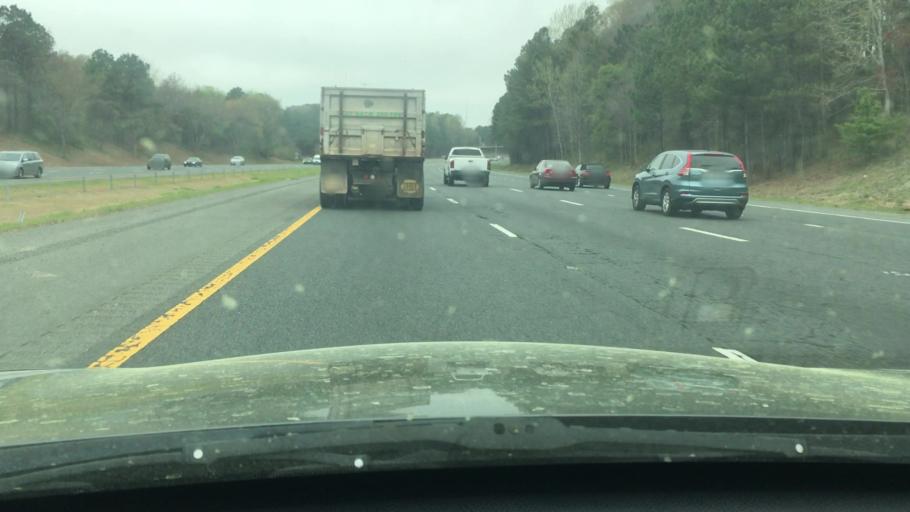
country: US
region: North Carolina
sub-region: Wake County
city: Cary
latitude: 35.7750
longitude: -78.7445
